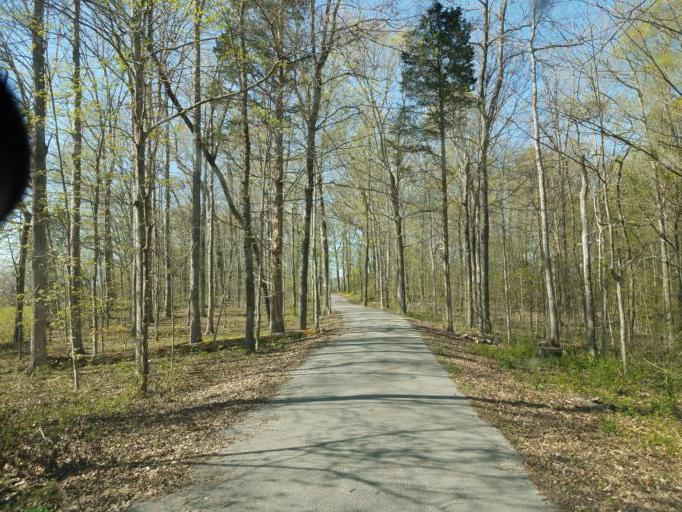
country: US
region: Kentucky
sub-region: Edmonson County
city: Brownsville
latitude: 37.1315
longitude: -86.1469
